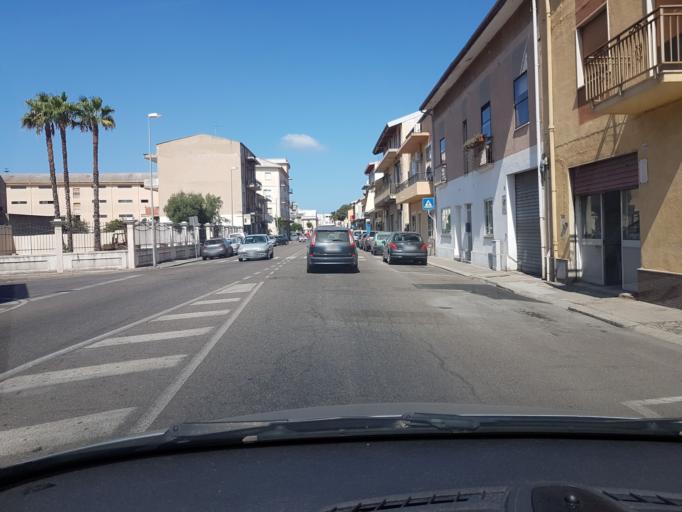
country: IT
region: Sardinia
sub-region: Provincia di Oristano
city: Oristano
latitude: 39.9078
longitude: 8.5990
